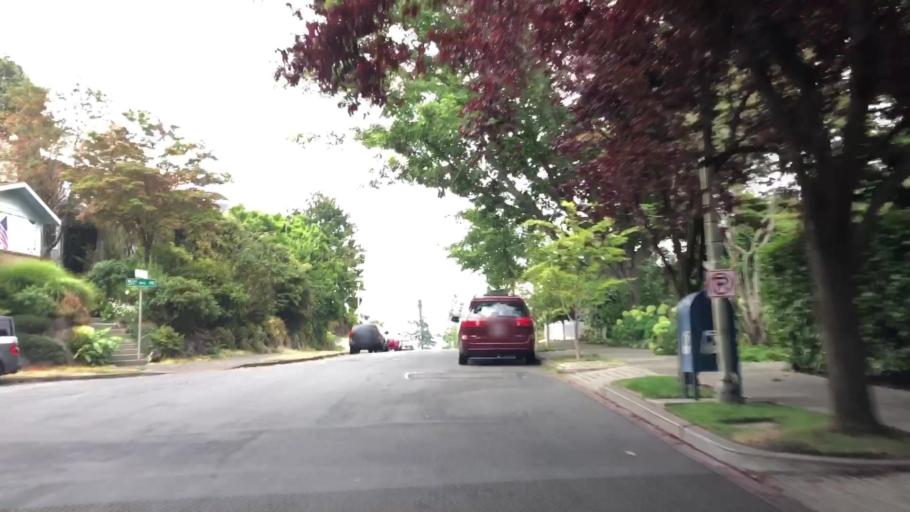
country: US
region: Washington
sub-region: King County
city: Yarrow Point
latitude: 47.6580
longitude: -122.2722
